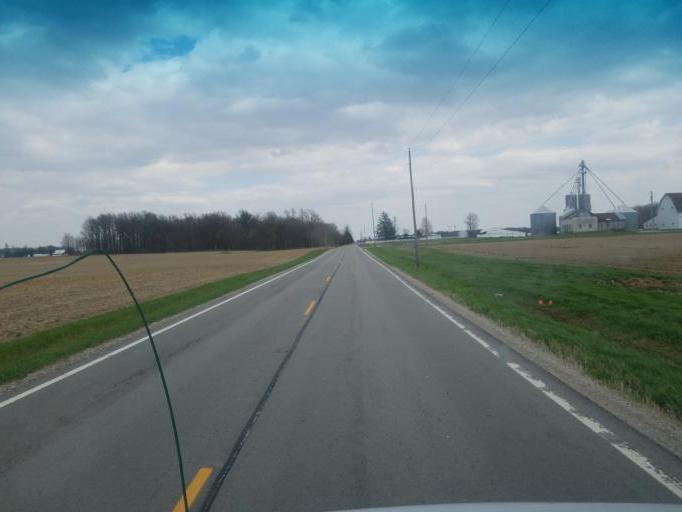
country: US
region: Ohio
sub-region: Crawford County
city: Bucyrus
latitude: 40.9504
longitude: -83.0300
